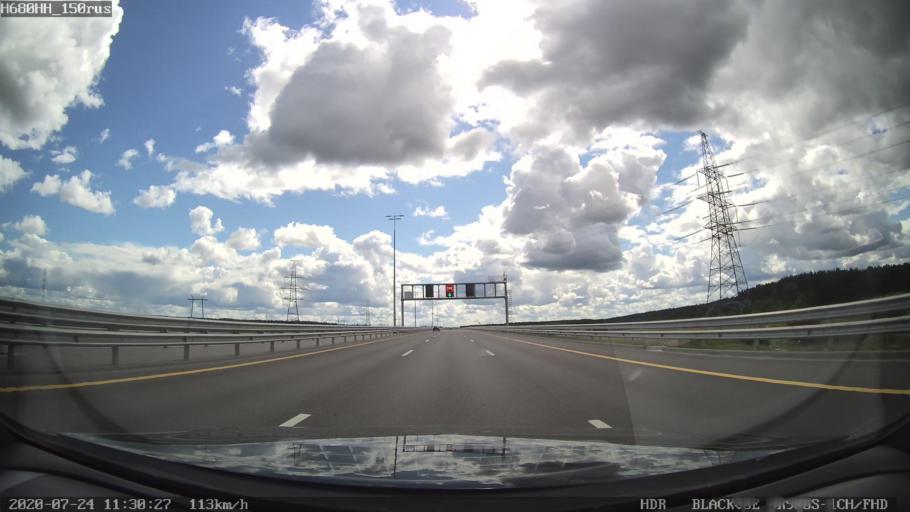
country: RU
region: Leningrad
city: Krasnyy Bor
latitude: 59.6692
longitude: 30.6132
